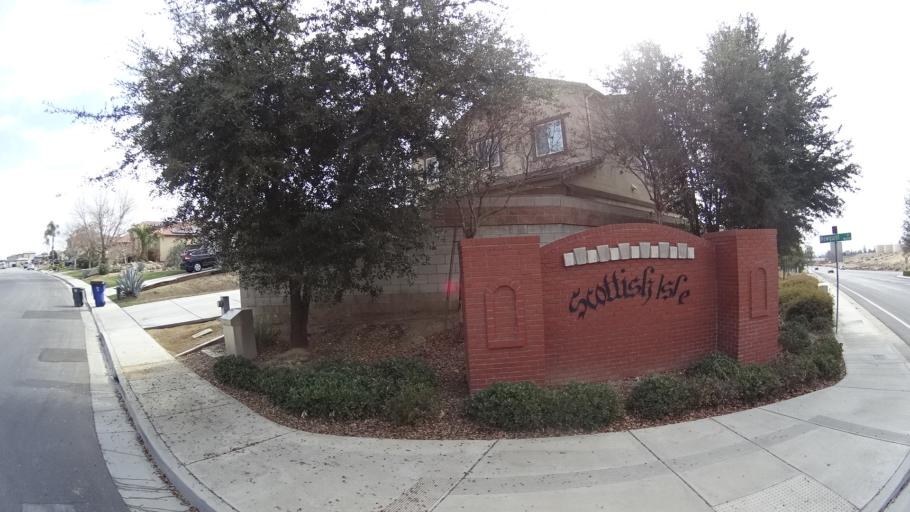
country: US
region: California
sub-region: Kern County
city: Bakersfield
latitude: 35.3874
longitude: -118.9290
